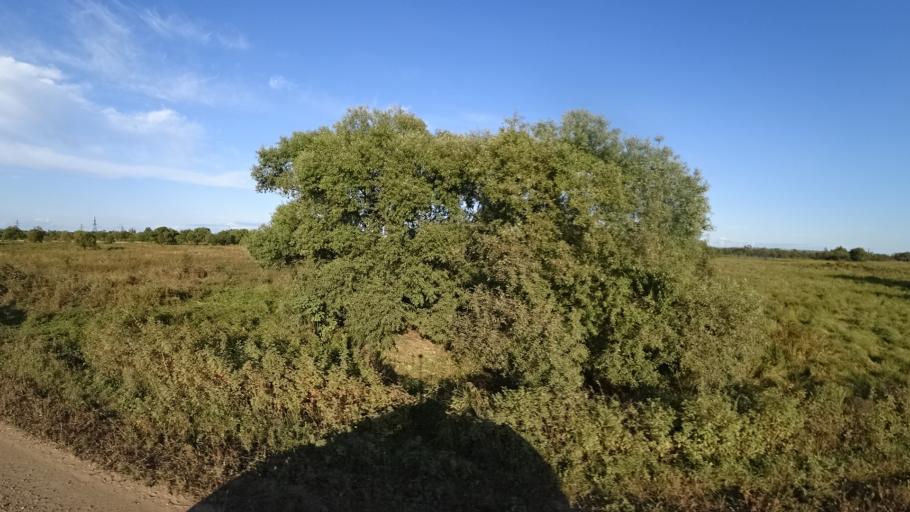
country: RU
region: Amur
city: Arkhara
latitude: 49.3615
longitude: 130.1368
